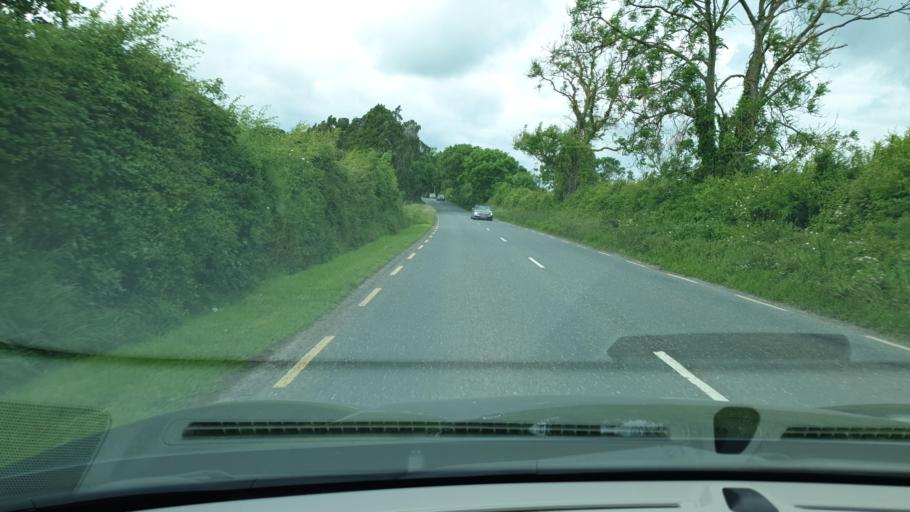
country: IE
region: Leinster
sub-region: An Mhi
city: Ashbourne
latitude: 53.4983
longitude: -6.4219
